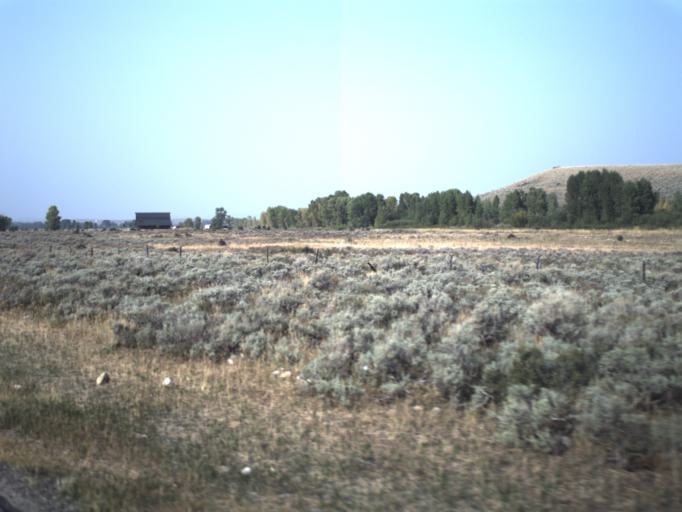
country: US
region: Wyoming
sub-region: Uinta County
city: Evanston
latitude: 40.9853
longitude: -110.8579
